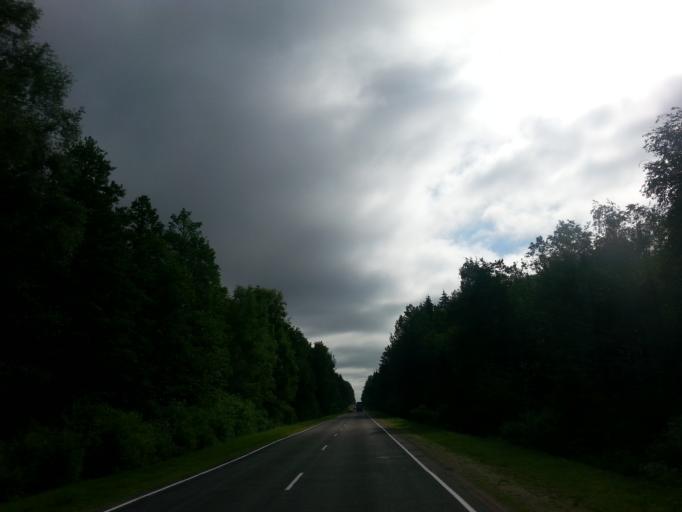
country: BY
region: Vitebsk
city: Mosar
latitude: 55.0829
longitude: 27.4570
